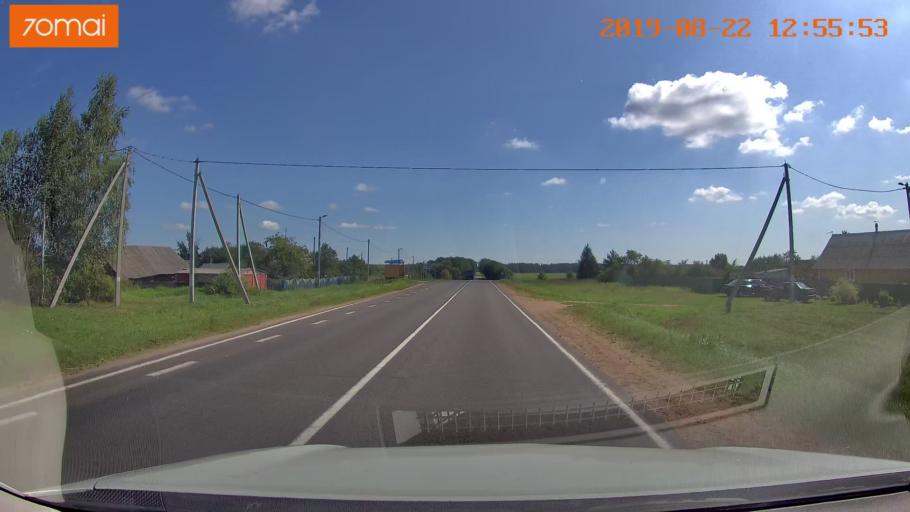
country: BY
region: Minsk
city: Prawdzinski
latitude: 53.4351
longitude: 27.7213
